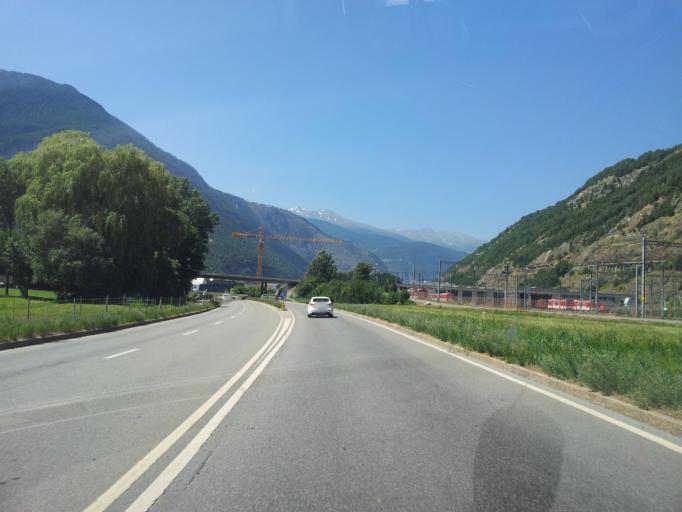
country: CH
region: Valais
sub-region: Brig District
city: Brig
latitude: 46.3134
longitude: 7.9702
